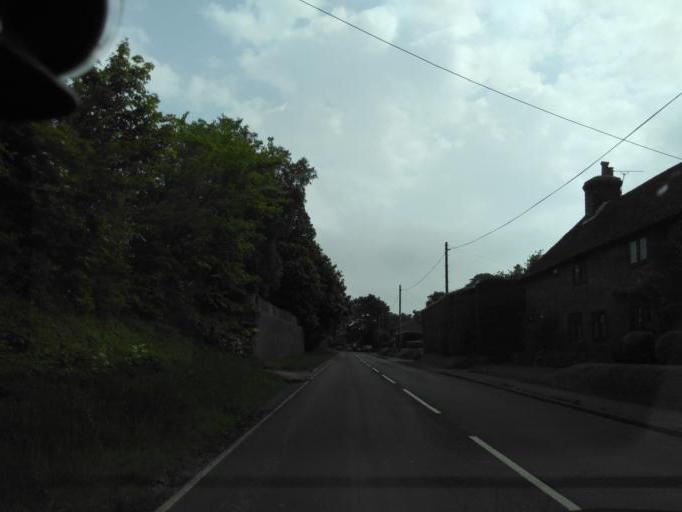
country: GB
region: England
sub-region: Kent
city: Canterbury
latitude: 51.2420
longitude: 1.0767
